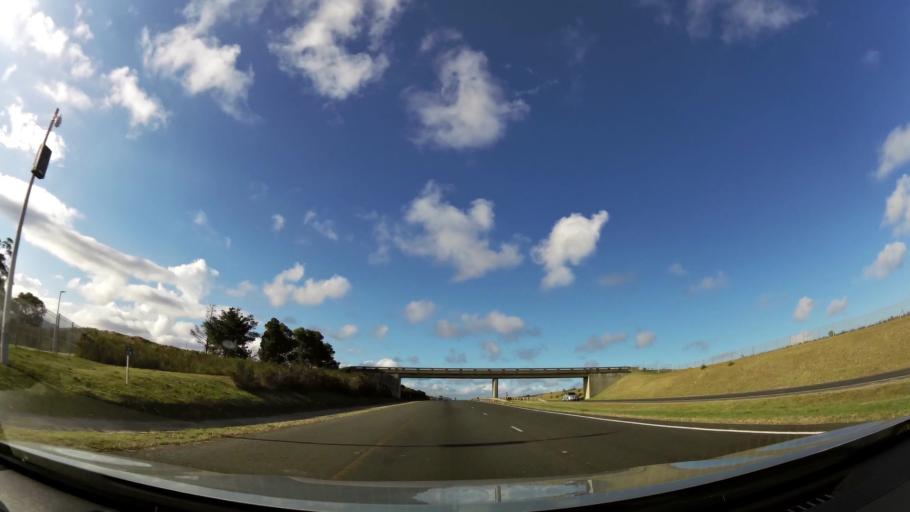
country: ZA
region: Western Cape
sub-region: Eden District Municipality
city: George
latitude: -33.9906
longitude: 22.4998
